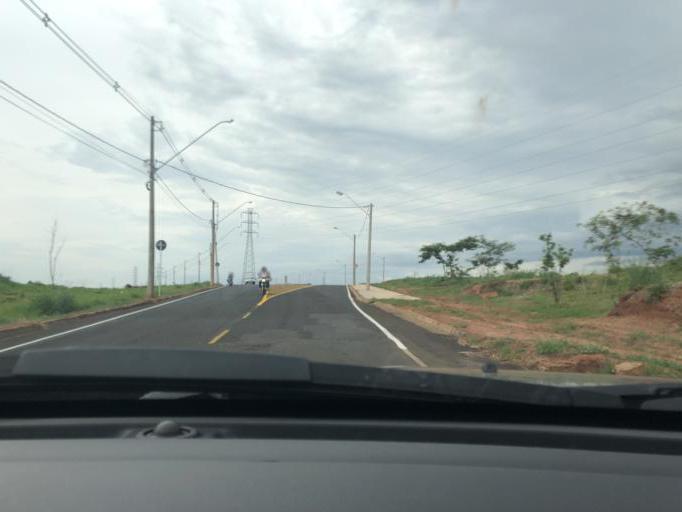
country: BR
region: Sao Paulo
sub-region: Sao Jose Do Rio Preto
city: Sao Jose do Rio Preto
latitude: -20.8339
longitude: -49.4245
